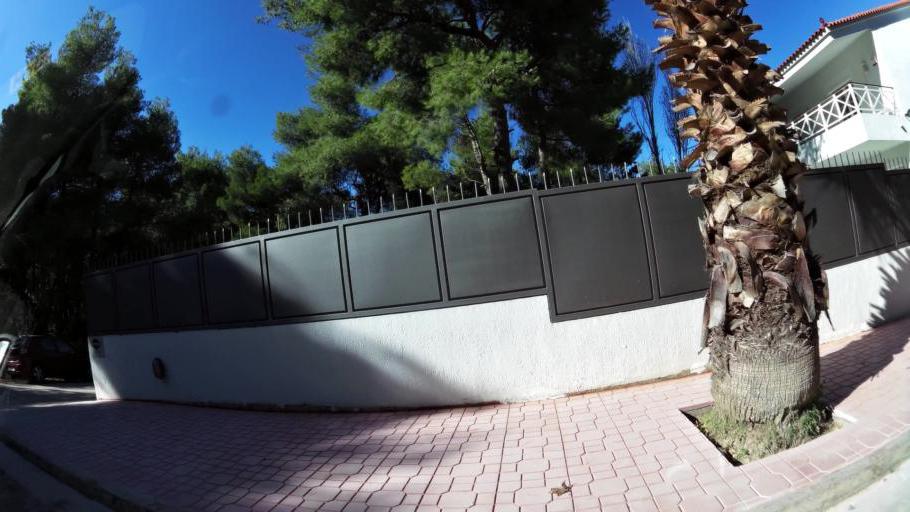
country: GR
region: Attica
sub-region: Nomarchia Anatolikis Attikis
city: Rodopoli
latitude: 38.1116
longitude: 23.8768
